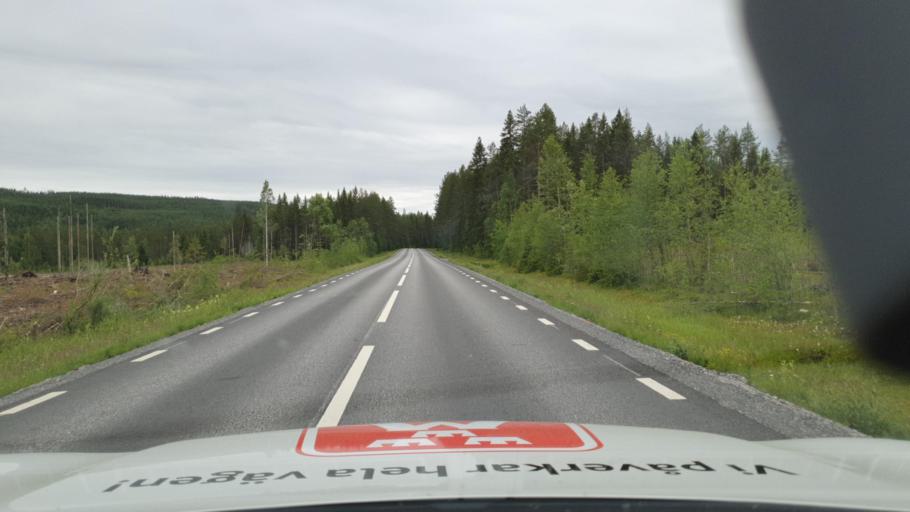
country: SE
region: Vaesterbotten
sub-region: Vannas Kommun
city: Vaennaes
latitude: 63.7299
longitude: 19.6518
